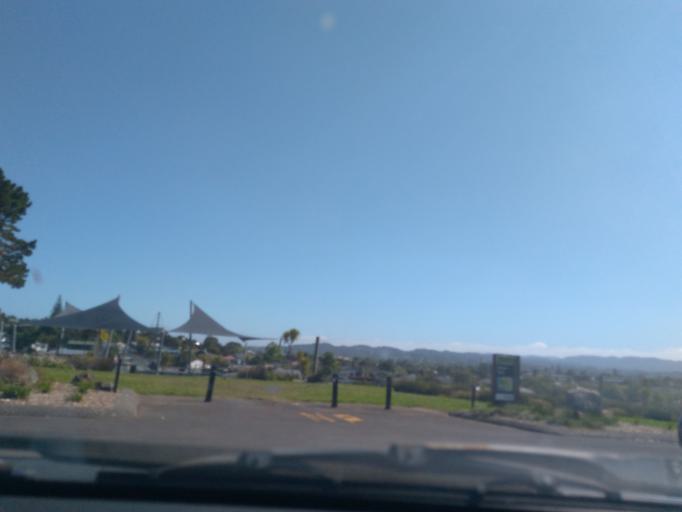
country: NZ
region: Auckland
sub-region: Auckland
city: Rosebank
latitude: -36.8855
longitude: 174.6992
